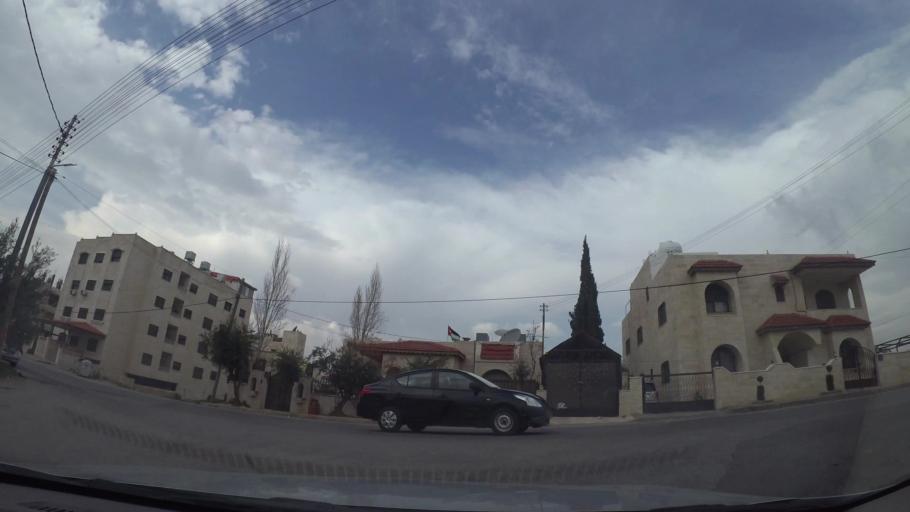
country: JO
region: Amman
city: Umm as Summaq
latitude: 31.8849
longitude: 35.8695
